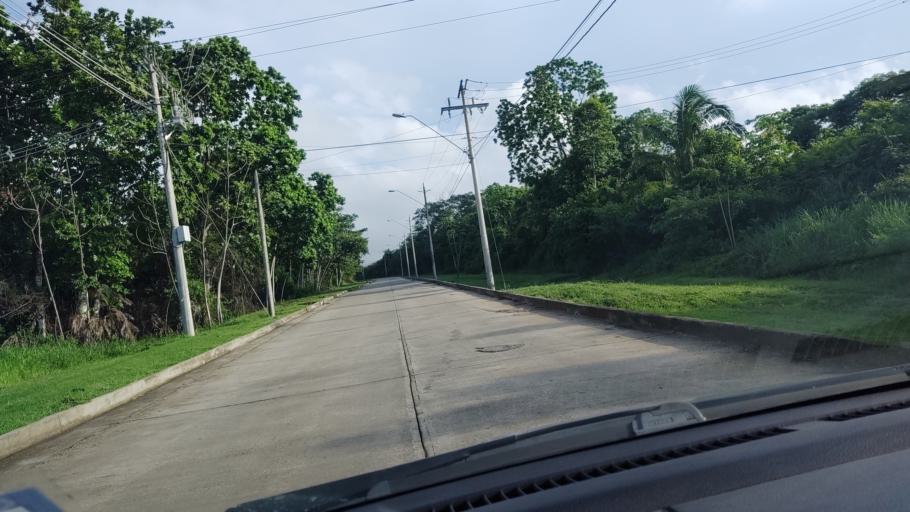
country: PA
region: Panama
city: Nuevo Arraijan
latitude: 8.9211
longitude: -79.7502
